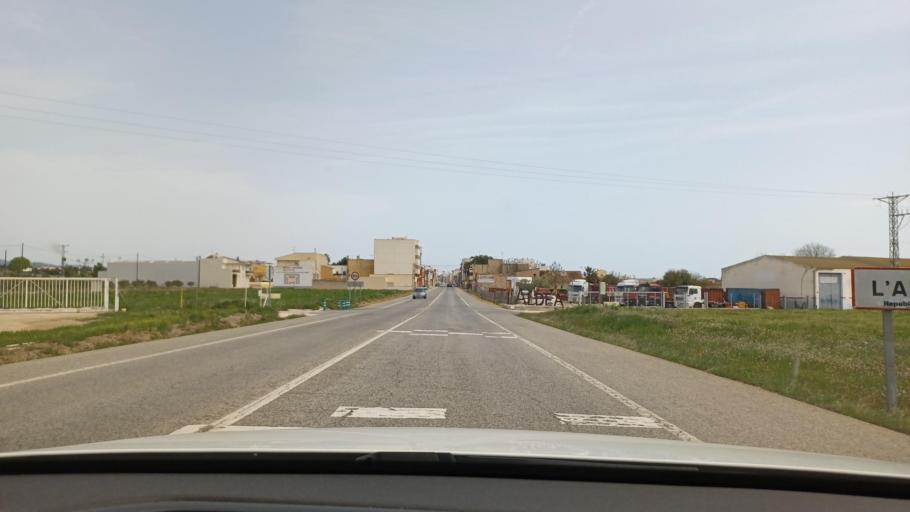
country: ES
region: Catalonia
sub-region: Provincia de Tarragona
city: Amposta
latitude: 40.7385
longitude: 0.6058
